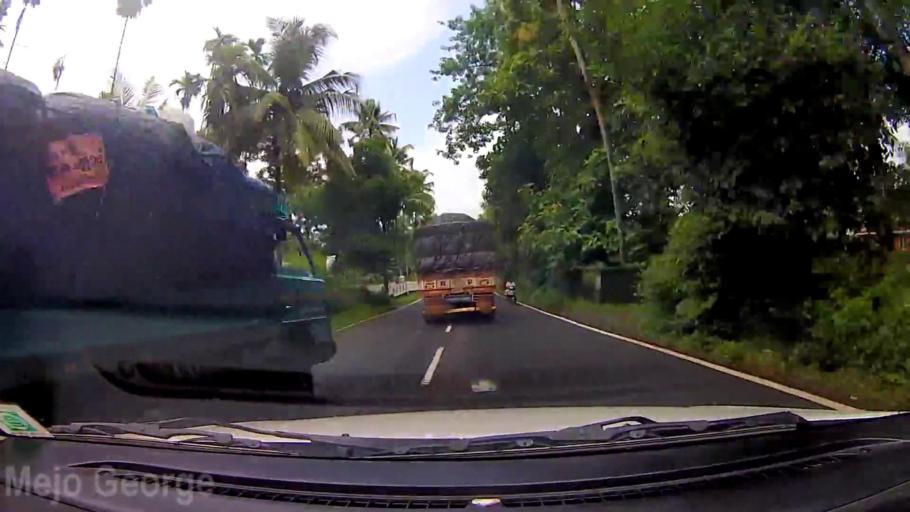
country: IN
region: Kerala
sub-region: Thrissur District
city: Kizhake Chalakudi
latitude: 10.3344
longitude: 76.3057
